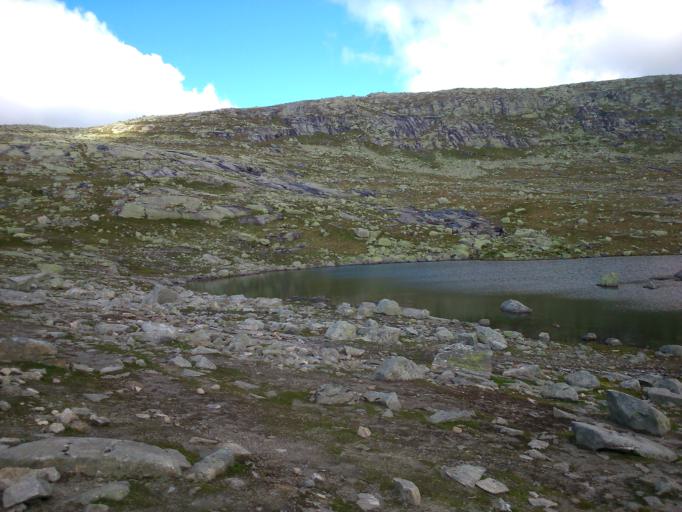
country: NO
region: Hordaland
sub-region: Odda
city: Odda
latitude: 60.1460
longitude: 6.6725
